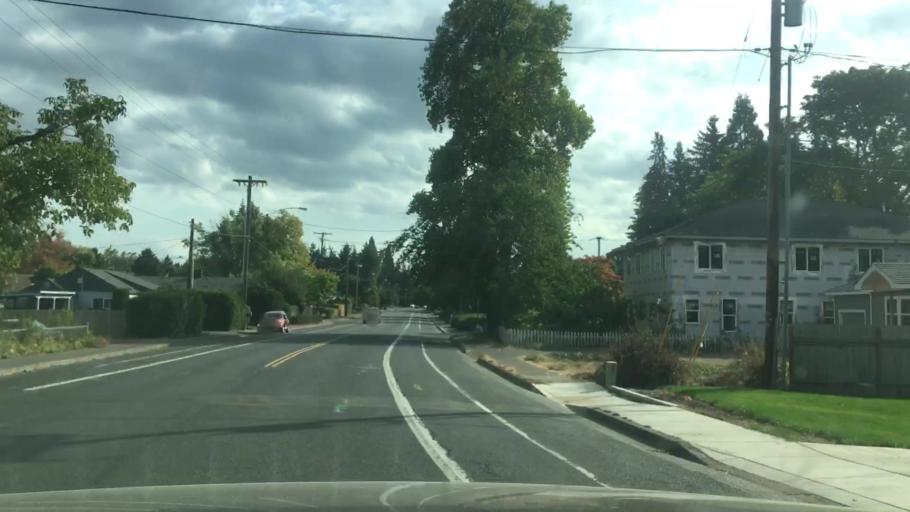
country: US
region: Oregon
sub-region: Lane County
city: Eugene
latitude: 44.0880
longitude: -123.0880
